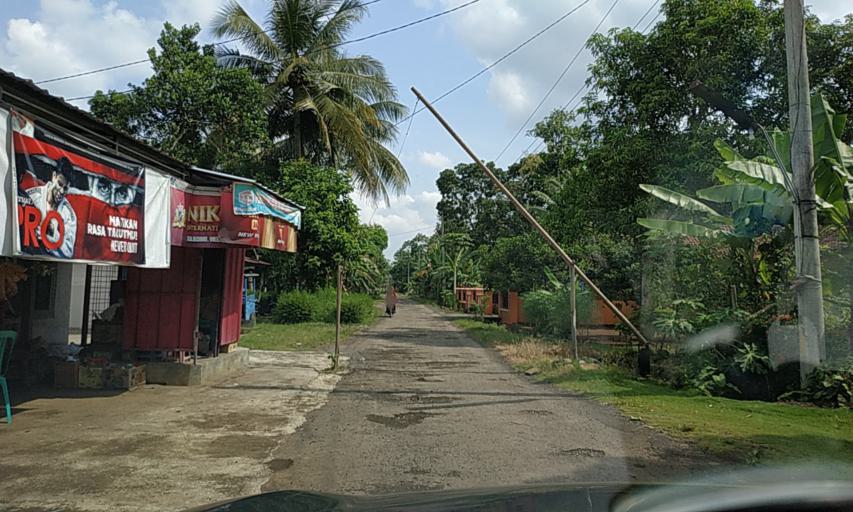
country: ID
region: Central Java
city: Bakung
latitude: -7.3438
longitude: 108.6670
